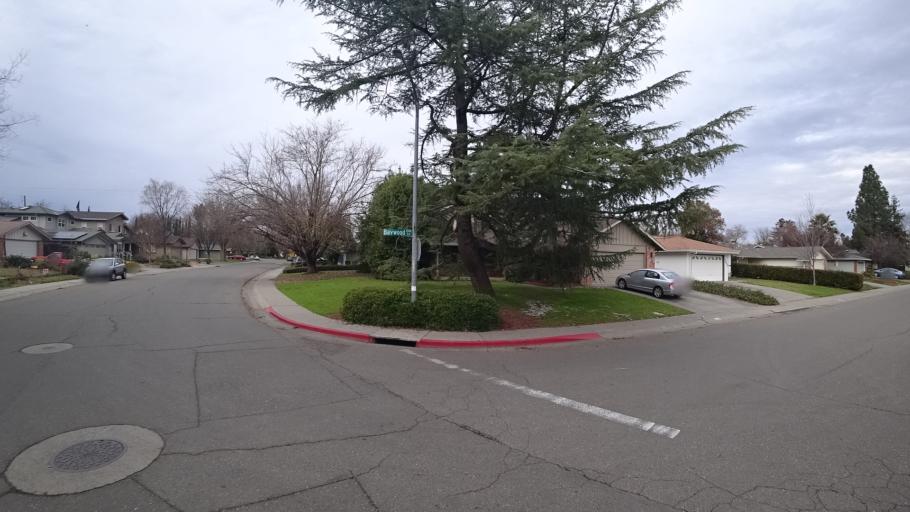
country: US
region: California
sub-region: Yolo County
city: Davis
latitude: 38.5598
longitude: -121.7245
